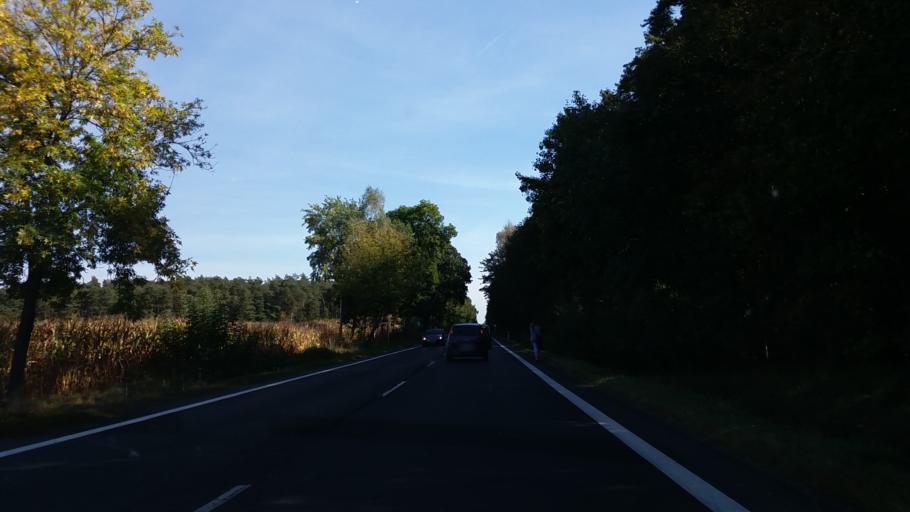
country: PL
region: Greater Poland Voivodeship
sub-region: Powiat miedzychodzki
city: Kwilcz
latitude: 52.5347
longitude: 16.1580
